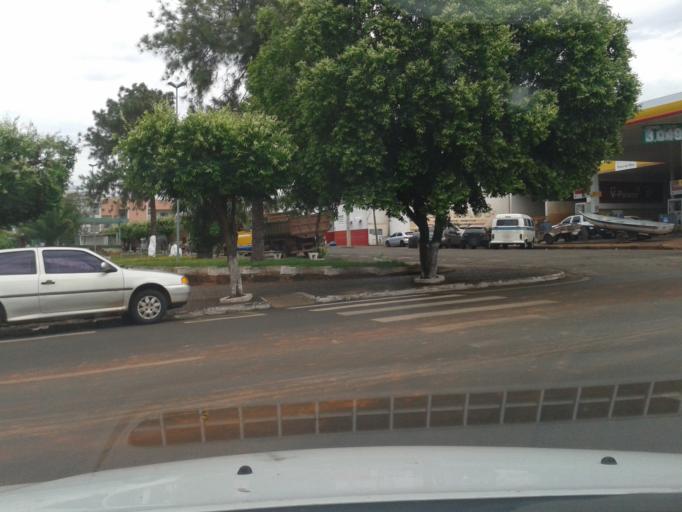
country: BR
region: Minas Gerais
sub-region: Iturama
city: Iturama
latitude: -19.7321
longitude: -50.1976
